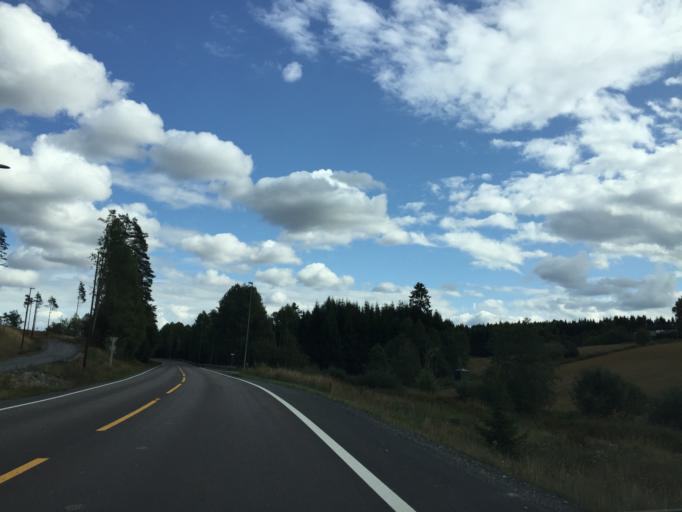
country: NO
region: Ostfold
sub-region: Hobol
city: Knappstad
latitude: 59.6206
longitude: 11.0079
